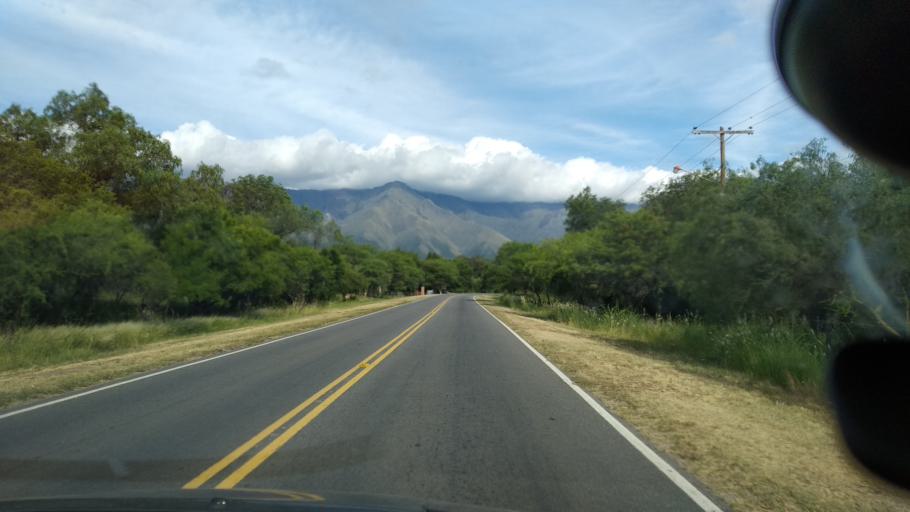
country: AR
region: Cordoba
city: Villa Las Rosas
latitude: -32.0102
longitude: -65.0505
